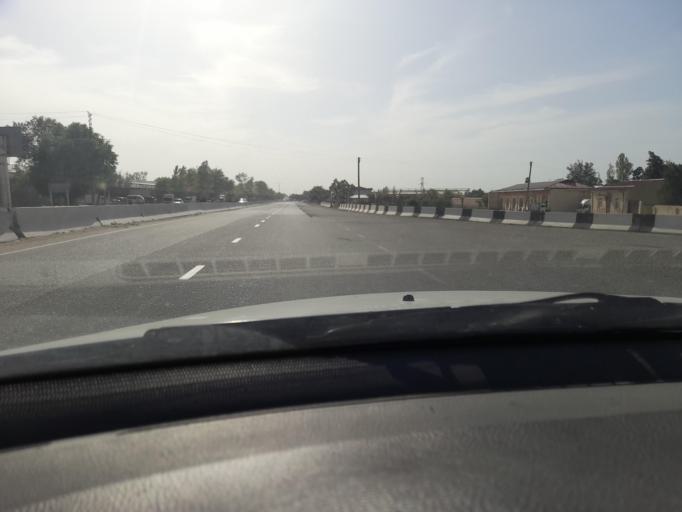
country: UZ
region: Samarqand
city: Kattaqo'rg'on
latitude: 39.9156
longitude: 66.3163
